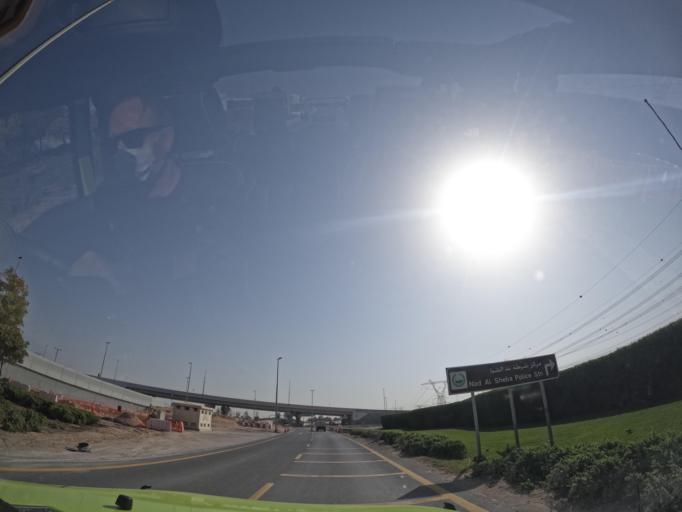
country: AE
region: Dubai
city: Dubai
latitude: 25.1701
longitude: 55.3166
